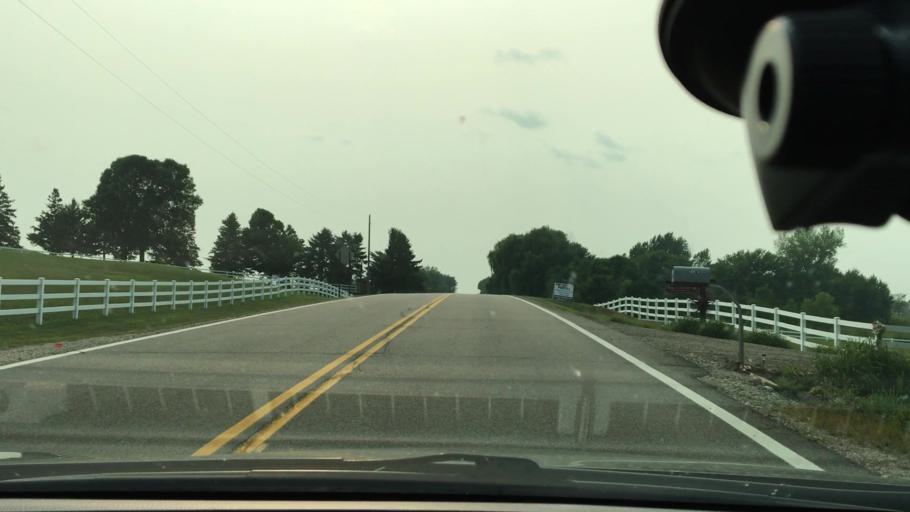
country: US
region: Minnesota
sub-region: Hennepin County
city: Dayton
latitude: 45.2523
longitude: -93.5403
